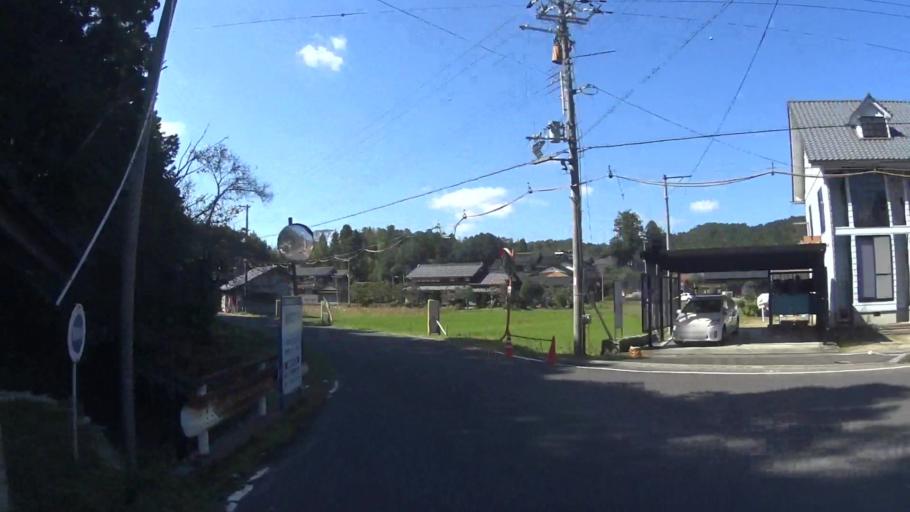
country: JP
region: Hyogo
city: Toyooka
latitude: 35.5951
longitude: 134.9460
